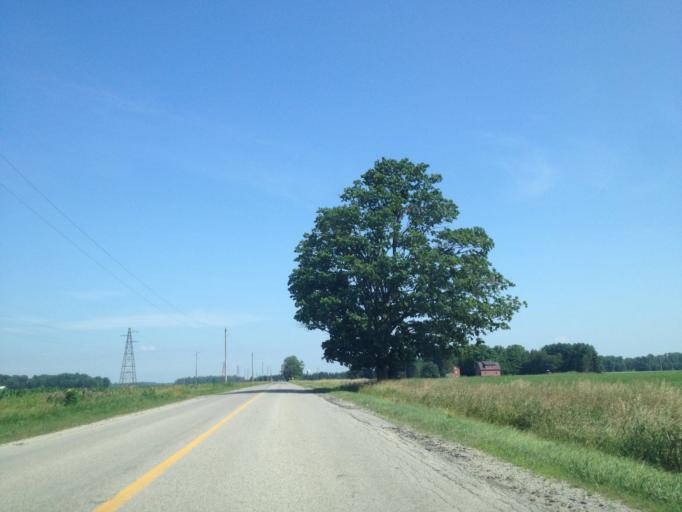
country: CA
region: Ontario
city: London
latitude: 43.0948
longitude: -81.2208
